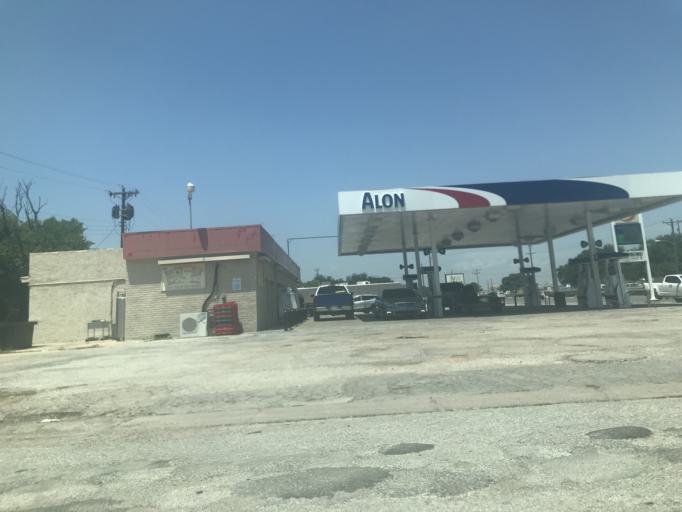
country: US
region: Texas
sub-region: Taylor County
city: Abilene
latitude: 32.4494
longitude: -99.7509
